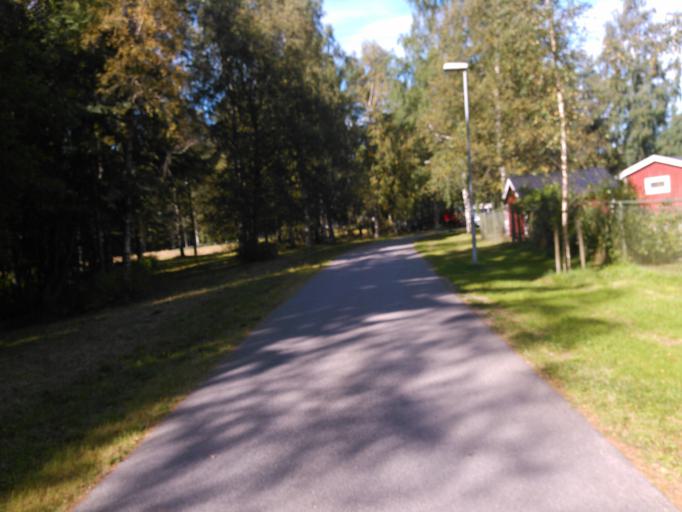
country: SE
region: Vaesterbotten
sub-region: Umea Kommun
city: Umea
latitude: 63.8042
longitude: 20.3111
